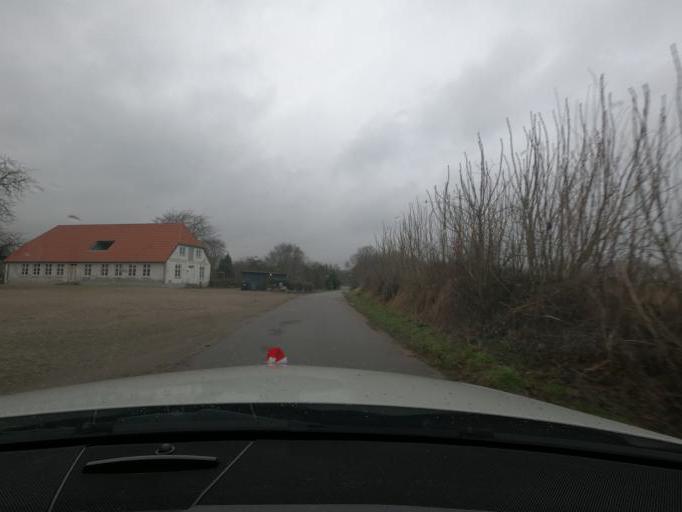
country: DK
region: South Denmark
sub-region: Haderslev Kommune
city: Starup
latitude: 55.2449
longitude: 9.6869
